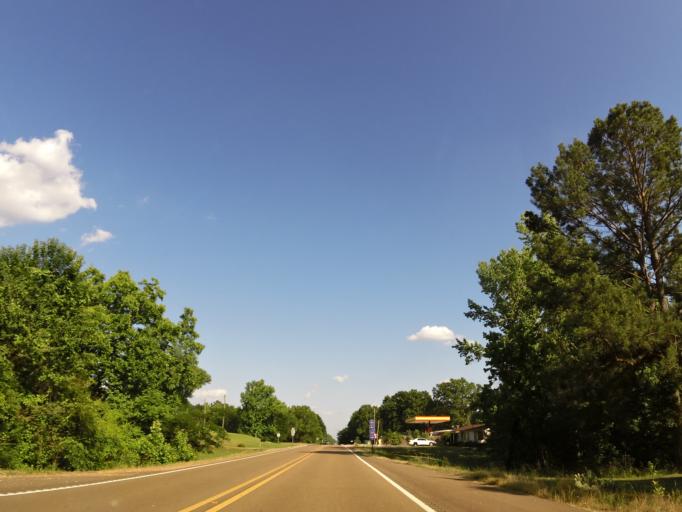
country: US
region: Mississippi
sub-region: Yalobusha County
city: Water Valley
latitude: 34.1775
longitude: -89.4584
